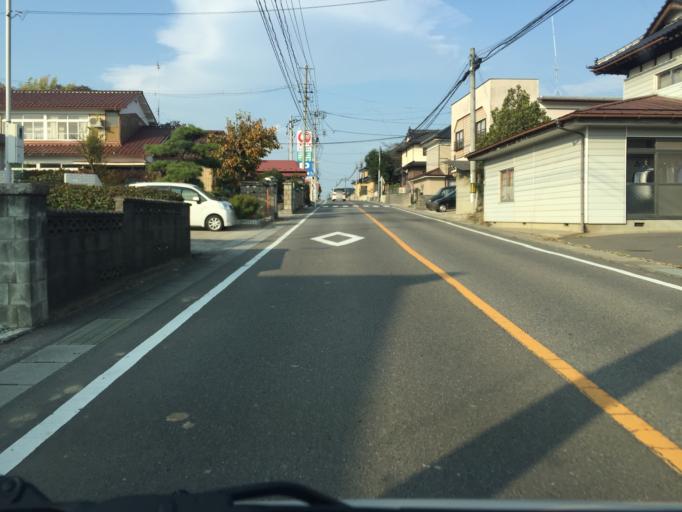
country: JP
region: Fukushima
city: Motomiya
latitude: 37.4921
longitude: 140.4012
